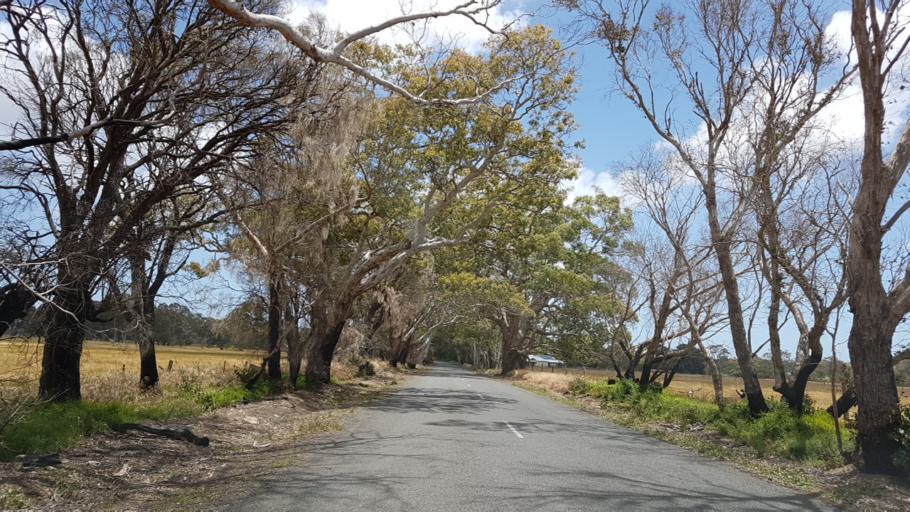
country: AU
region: South Australia
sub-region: Onkaparinga
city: Aldinga
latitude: -35.3773
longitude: 138.4907
